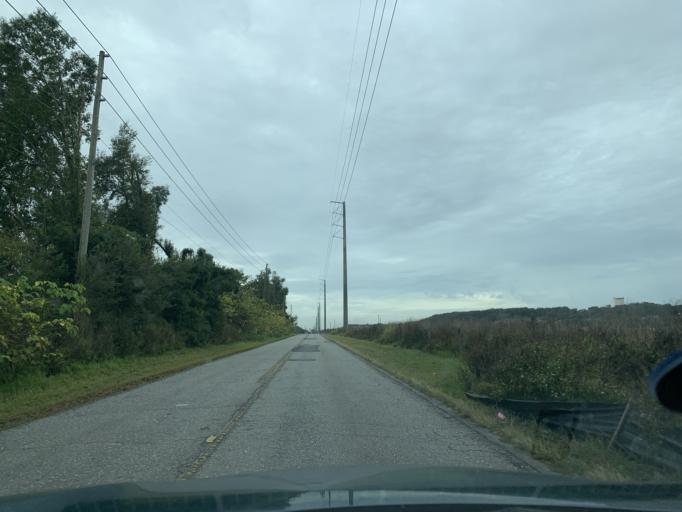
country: US
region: Florida
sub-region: Pasco County
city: Zephyrhills North
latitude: 28.2697
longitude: -82.1799
